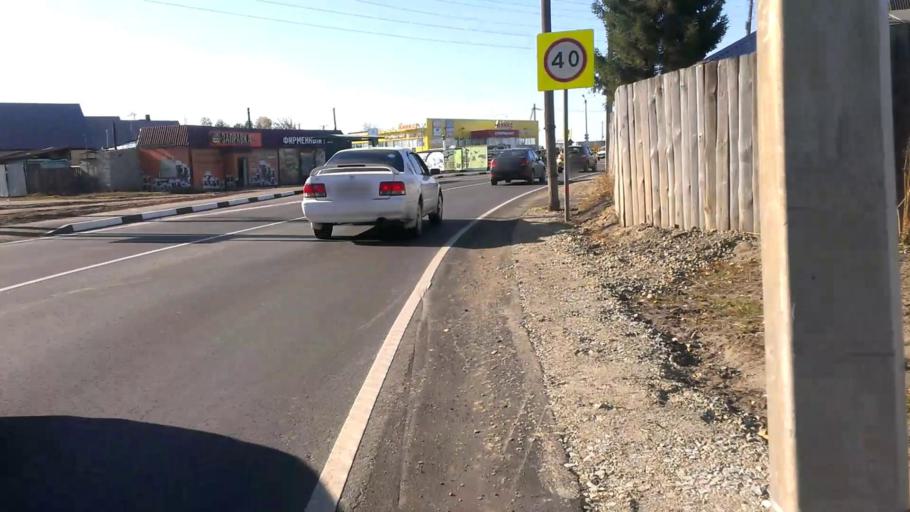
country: RU
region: Altai Krai
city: Sannikovo
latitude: 53.3178
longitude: 83.9459
